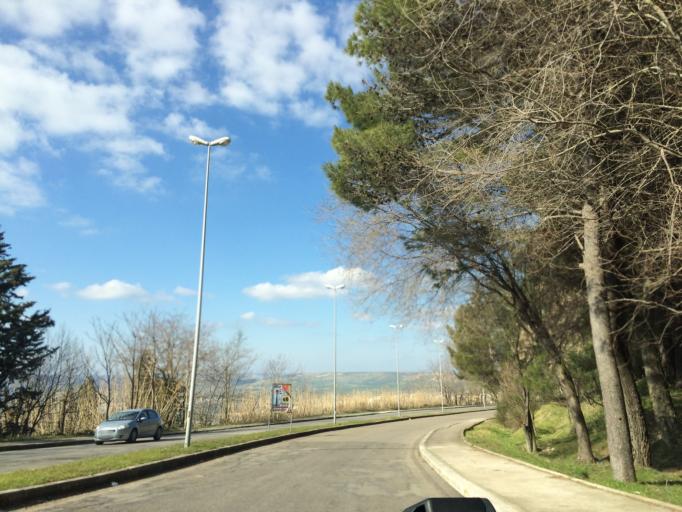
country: IT
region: Basilicate
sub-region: Provincia di Matera
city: Matera
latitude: 40.6662
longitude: 16.5902
